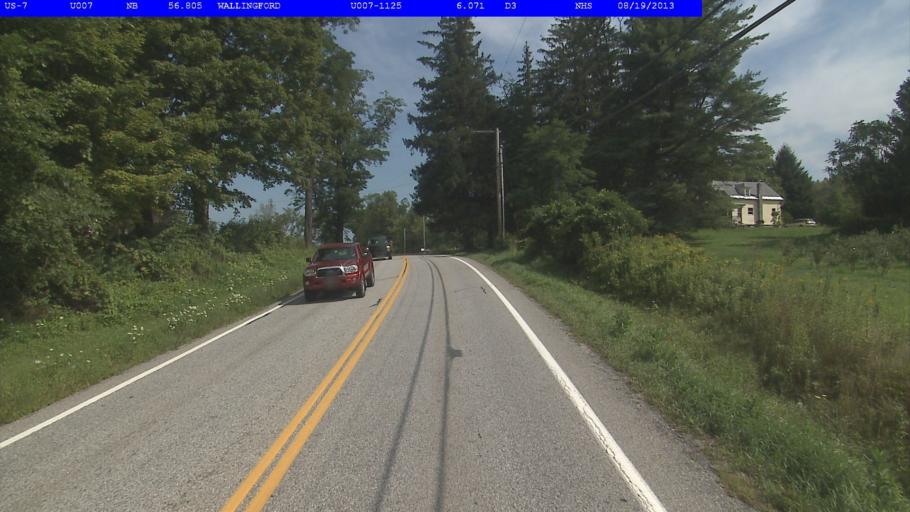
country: US
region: Vermont
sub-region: Rutland County
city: Rutland
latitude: 43.4799
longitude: -72.9747
